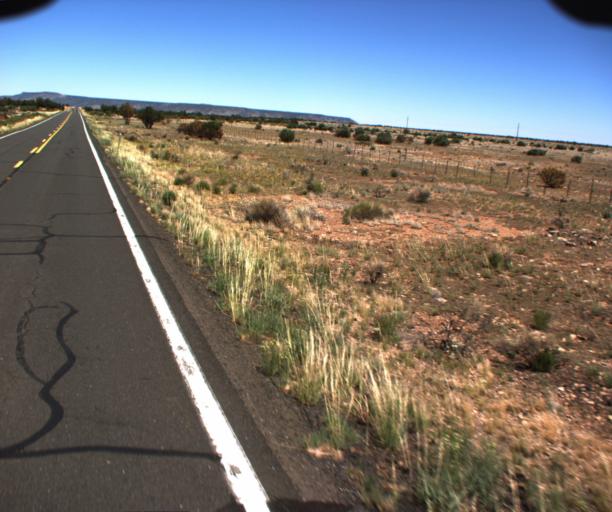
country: US
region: Arizona
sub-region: Coconino County
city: LeChee
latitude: 34.7581
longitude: -111.0261
